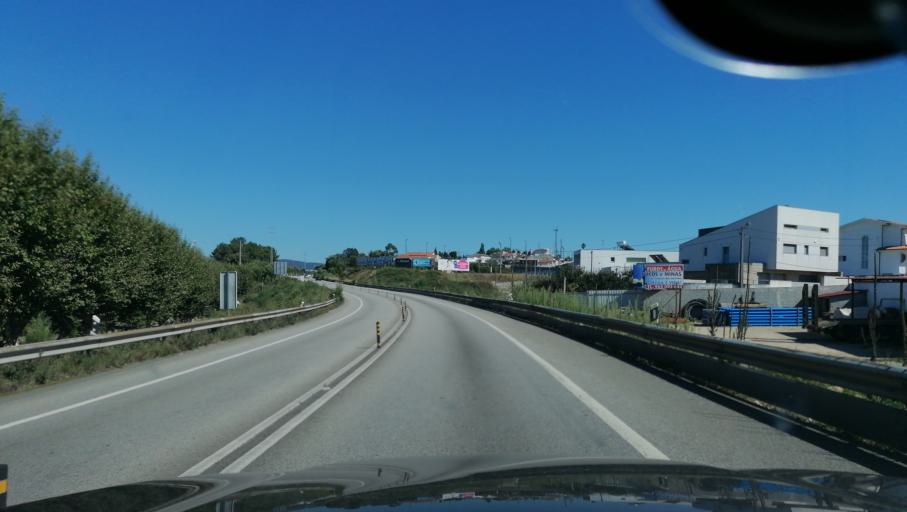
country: PT
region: Aveiro
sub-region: Santa Maria da Feira
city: Arrifana
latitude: 40.9208
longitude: -8.4998
